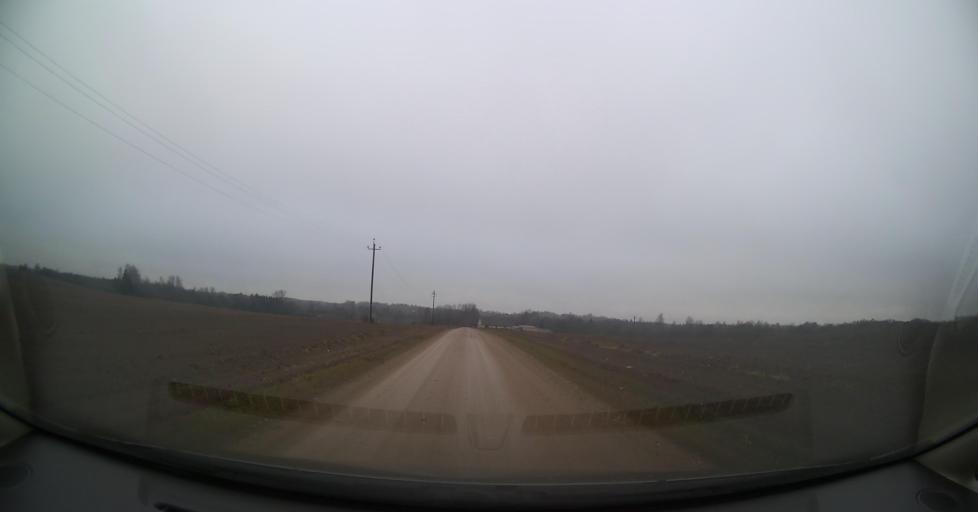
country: EE
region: Tartu
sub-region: Tartu linn
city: Tartu
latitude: 58.3885
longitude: 26.9981
